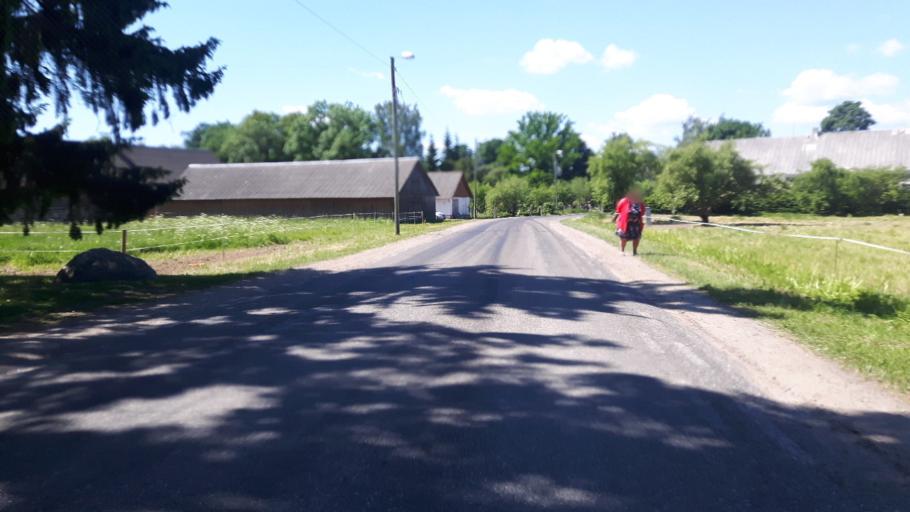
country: EE
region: Paernumaa
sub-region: Tootsi vald
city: Tootsi
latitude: 58.4811
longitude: 24.8141
